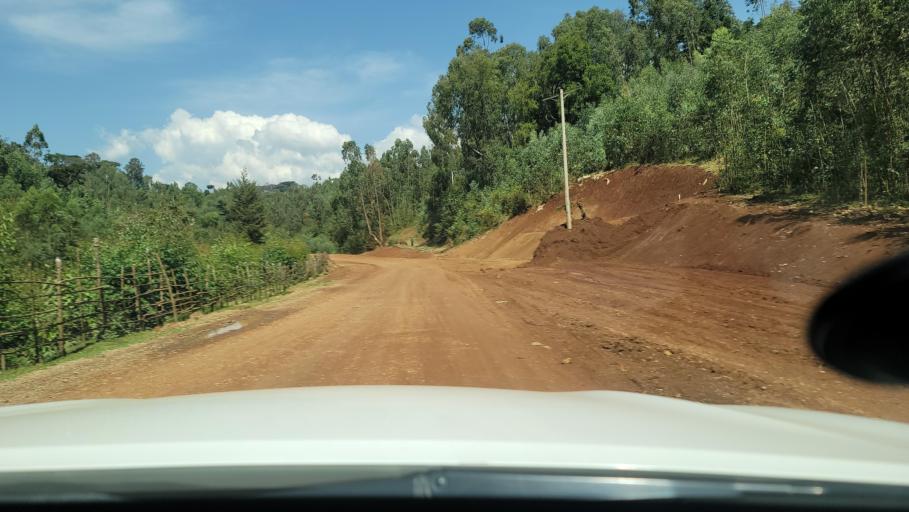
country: ET
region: Oromiya
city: Agaro
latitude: 7.8003
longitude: 36.4704
